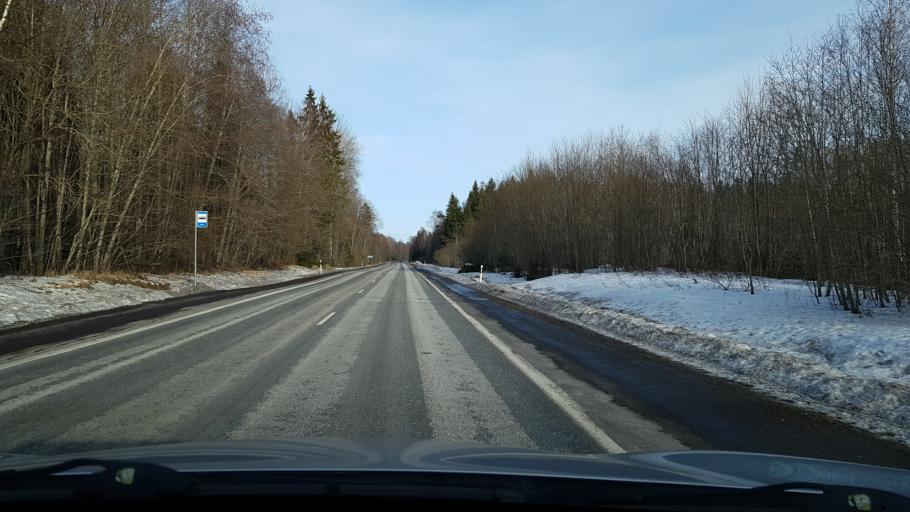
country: EE
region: Viljandimaa
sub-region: Abja vald
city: Abja-Paluoja
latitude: 58.3454
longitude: 25.3591
